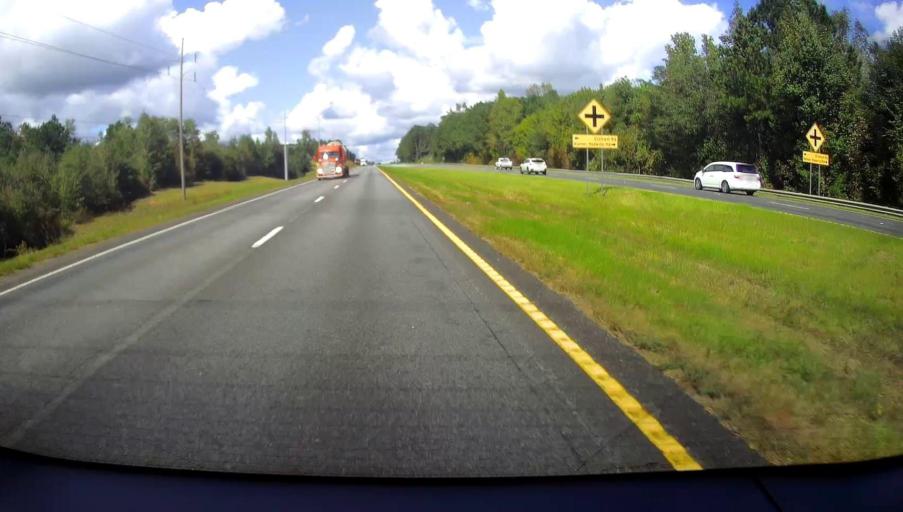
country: US
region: Georgia
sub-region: Jones County
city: Gray
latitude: 32.9596
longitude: -83.5808
